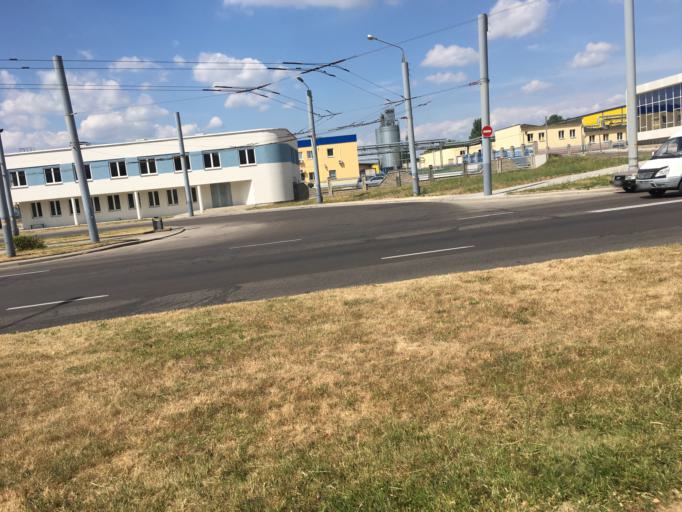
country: BY
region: Grodnenskaya
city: Hrodna
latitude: 53.7129
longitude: 23.8401
